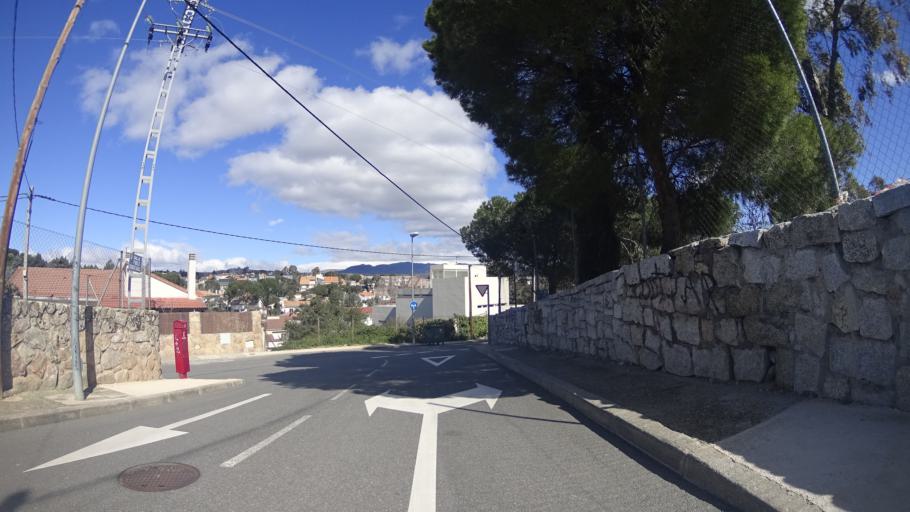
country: ES
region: Madrid
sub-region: Provincia de Madrid
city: Las Matas
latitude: 40.5556
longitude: -3.8931
